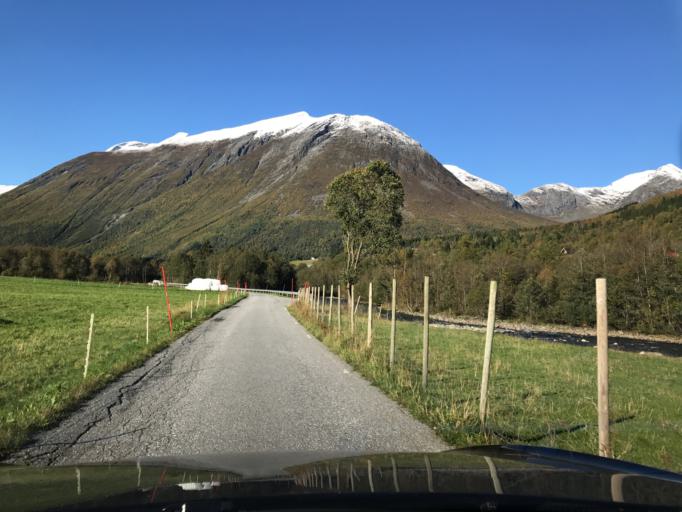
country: NO
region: More og Romsdal
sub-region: Norddal
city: Valldal
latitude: 62.3308
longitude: 7.3760
